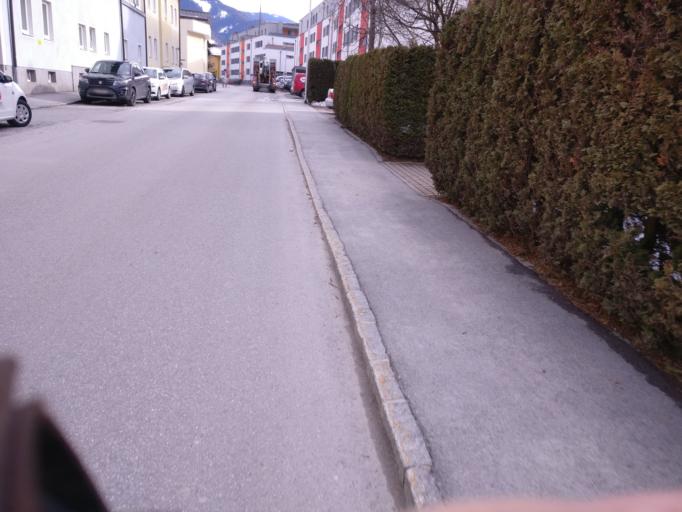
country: AT
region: Salzburg
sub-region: Politischer Bezirk Sankt Johann im Pongau
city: Bischofshofen
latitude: 47.4187
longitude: 13.2149
